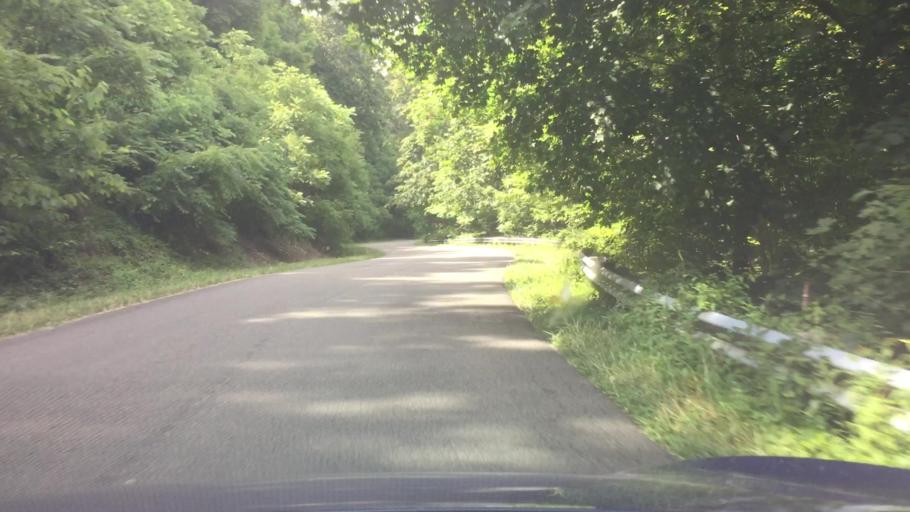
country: US
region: Virginia
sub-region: Wythe County
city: Wytheville
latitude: 36.9304
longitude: -81.0685
